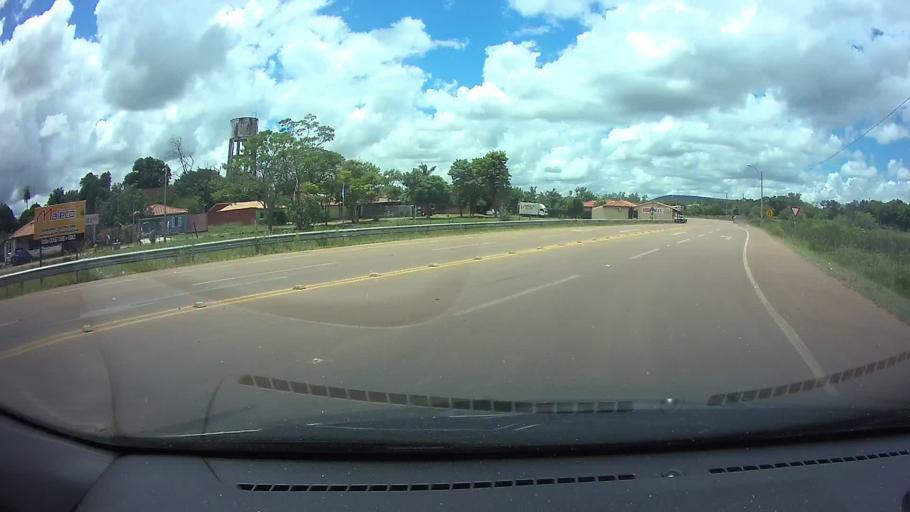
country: PY
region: Paraguari
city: La Colmena
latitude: -25.8926
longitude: -56.8443
